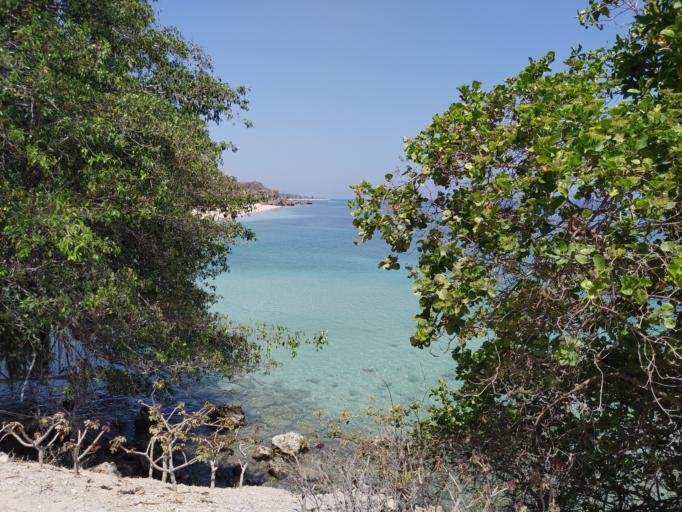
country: TL
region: Baucau
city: Baucau
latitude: -8.4408
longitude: 126.4659
